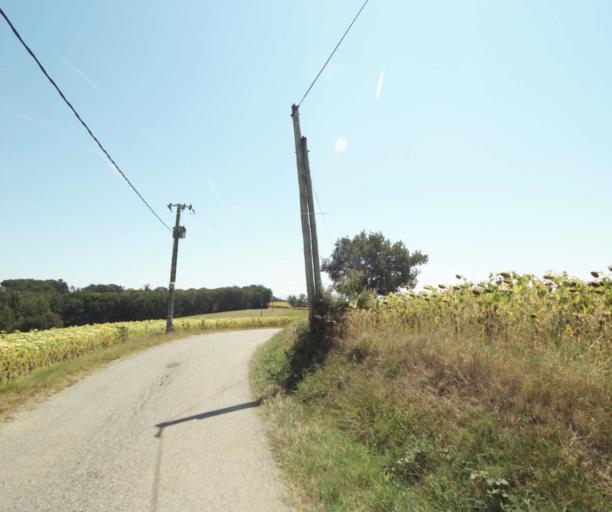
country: FR
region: Midi-Pyrenees
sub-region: Departement de l'Ariege
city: Lezat-sur-Leze
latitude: 43.2824
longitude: 1.3044
